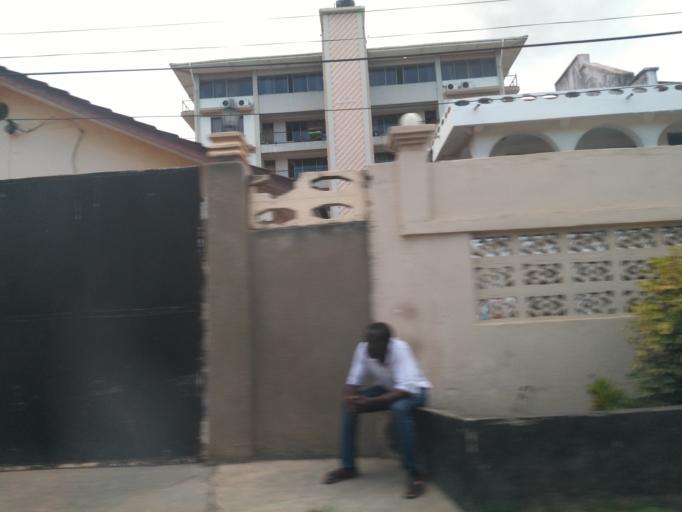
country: TZ
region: Dar es Salaam
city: Magomeni
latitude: -6.7653
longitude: 39.2666
